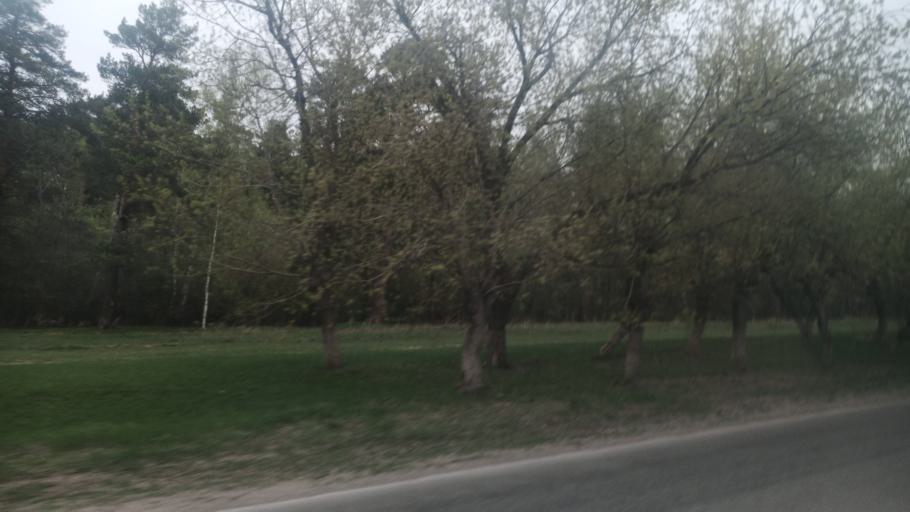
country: RU
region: Altai Krai
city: Yuzhnyy
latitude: 53.2570
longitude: 83.6890
